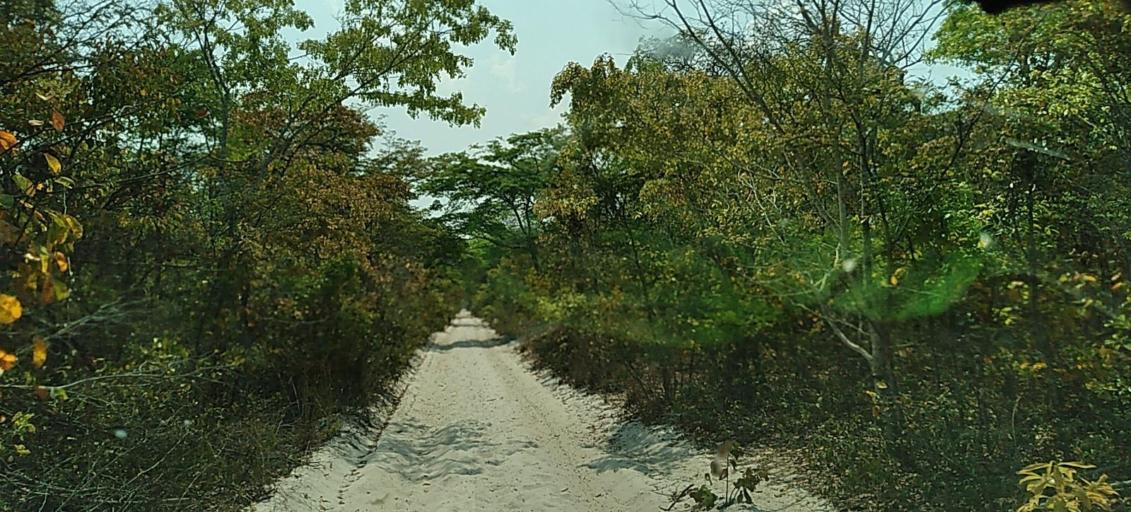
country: ZM
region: North-Western
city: Kabompo
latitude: -13.3906
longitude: 23.7832
